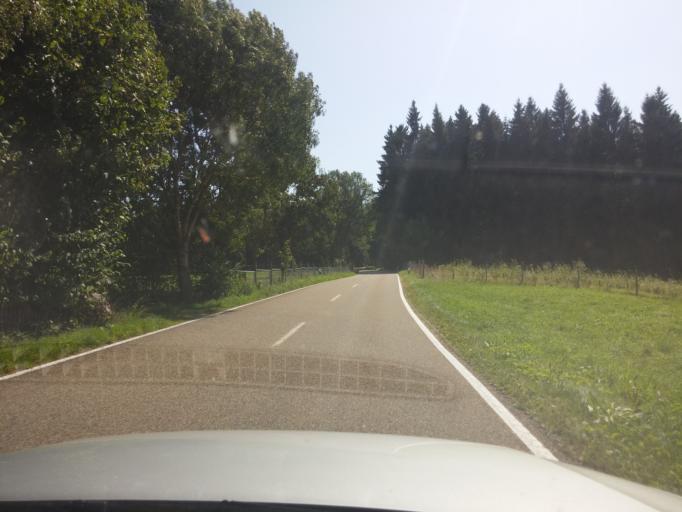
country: DE
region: Baden-Wuerttemberg
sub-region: Tuebingen Region
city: Aichstetten
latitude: 47.8527
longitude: 10.0582
